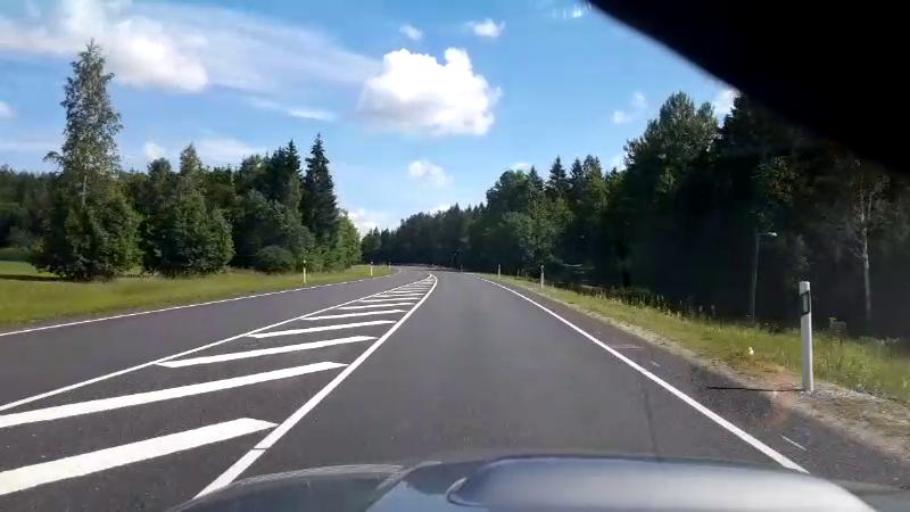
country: EE
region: Jaervamaa
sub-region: Jaerva-Jaani vald
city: Jarva-Jaani
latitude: 59.1283
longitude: 25.7475
